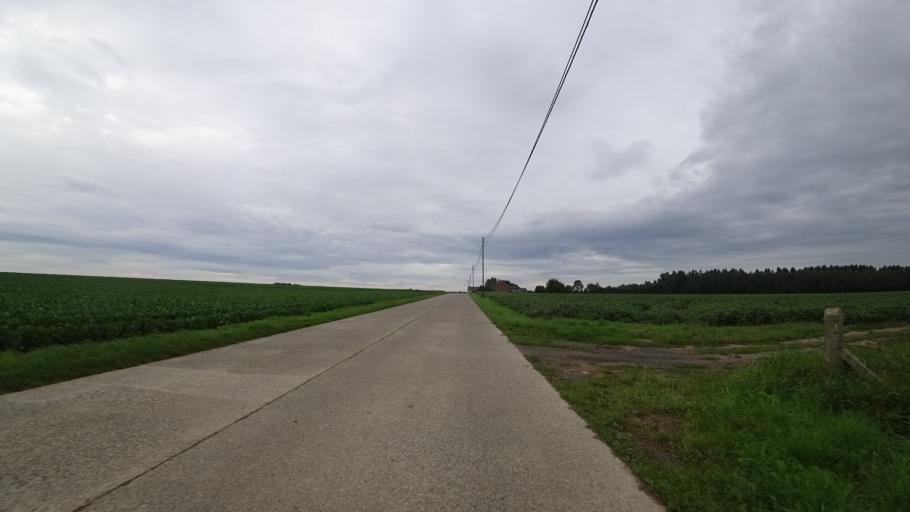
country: BE
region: Wallonia
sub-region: Province du Brabant Wallon
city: Perwez
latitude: 50.5667
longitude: 4.7845
